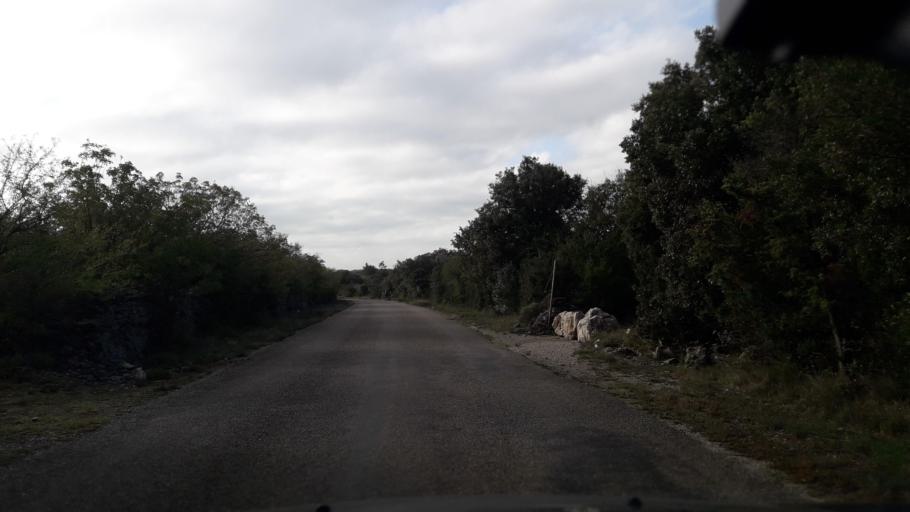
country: FR
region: Languedoc-Roussillon
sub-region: Departement du Gard
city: Saint-Julien-de-Peyrolas
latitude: 44.3525
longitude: 4.5283
